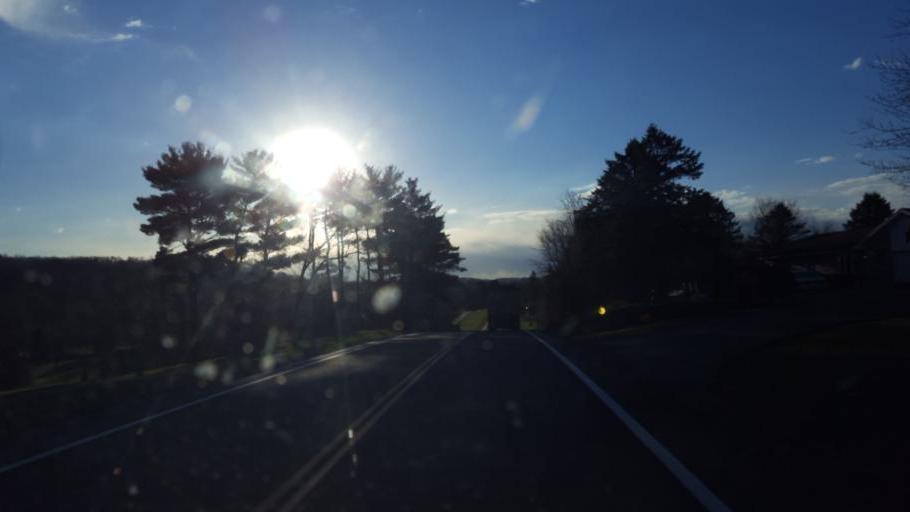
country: US
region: Ohio
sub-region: Ashland County
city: Loudonville
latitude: 40.6498
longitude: -82.2528
